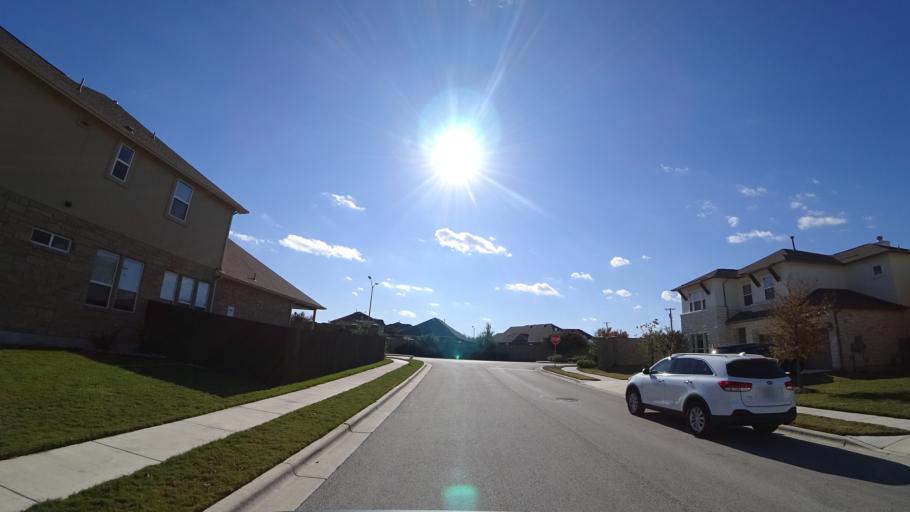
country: US
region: Texas
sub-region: Williamson County
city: Brushy Creek
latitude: 30.4927
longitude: -97.7234
